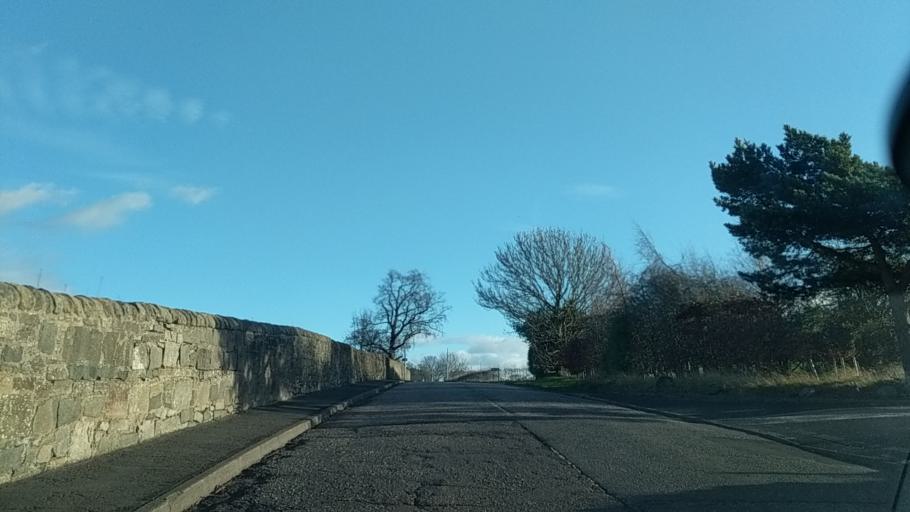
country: GB
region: Scotland
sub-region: Edinburgh
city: Queensferry
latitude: 55.9895
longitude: -3.3785
